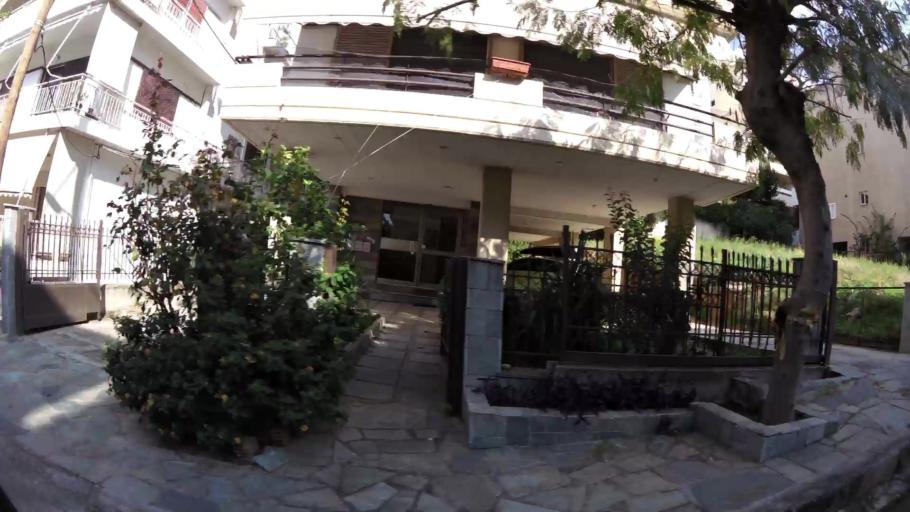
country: GR
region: Attica
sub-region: Nomarchia Athinas
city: Ilioupoli
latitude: 37.9250
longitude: 23.7631
